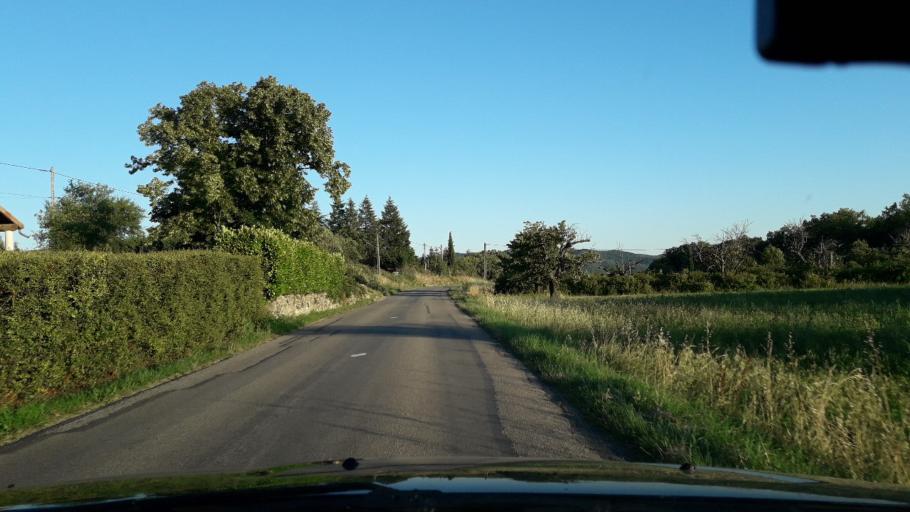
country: FR
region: Rhone-Alpes
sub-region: Departement de l'Ardeche
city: Lavilledieu
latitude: 44.5901
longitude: 4.4602
